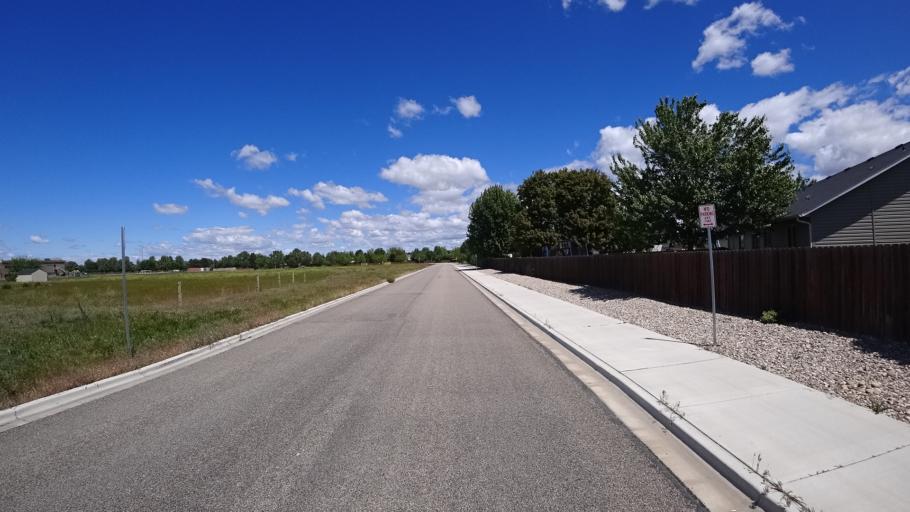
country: US
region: Idaho
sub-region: Ada County
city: Meridian
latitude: 43.6386
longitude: -116.3496
